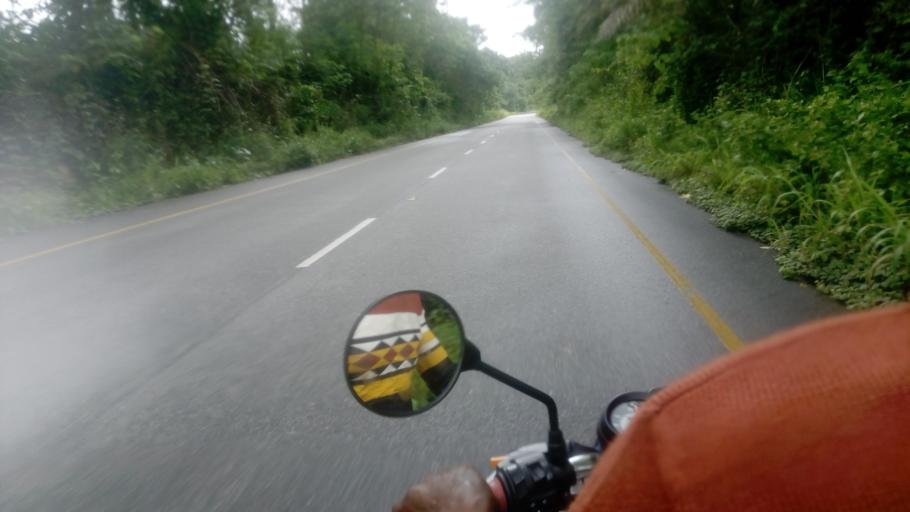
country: SL
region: Northern Province
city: Makali
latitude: 8.6342
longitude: -11.6760
